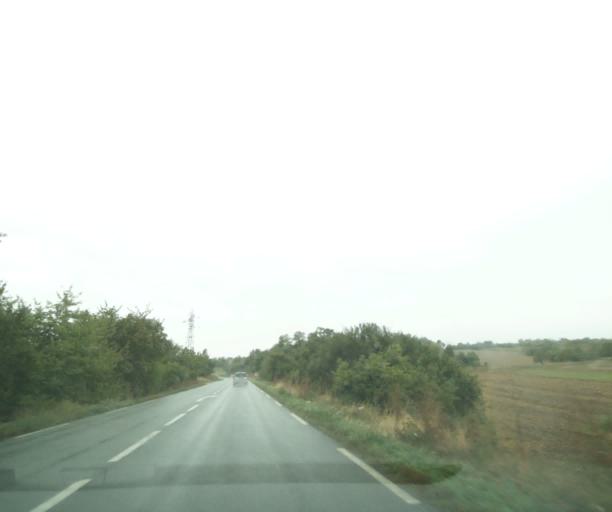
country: FR
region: Auvergne
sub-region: Departement du Puy-de-Dome
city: Cebazat
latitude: 45.8454
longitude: 3.1060
